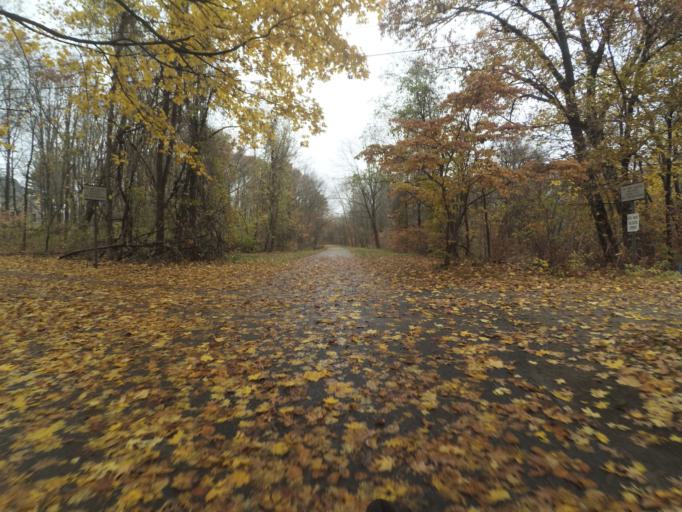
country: US
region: Massachusetts
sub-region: Middlesex County
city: Lexington
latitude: 42.4434
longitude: -71.2154
